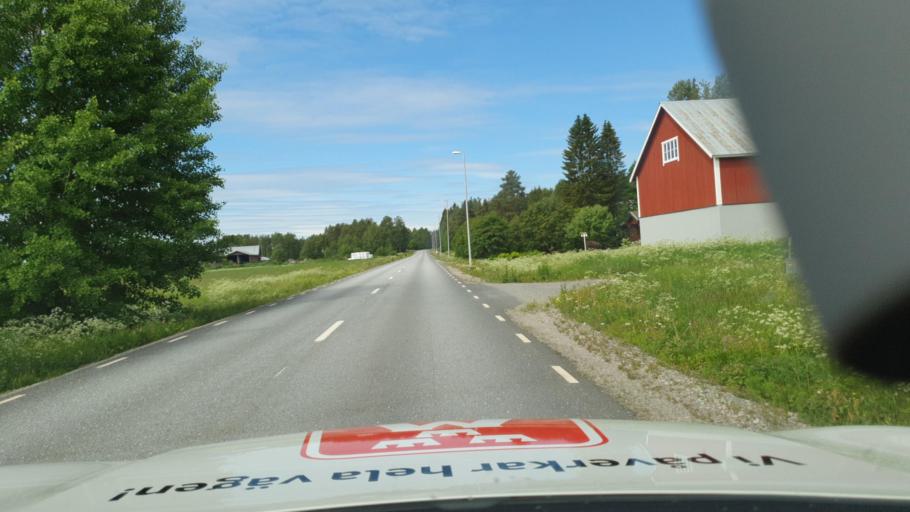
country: SE
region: Vaesterbotten
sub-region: Skelleftea Kommun
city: Forsbacka
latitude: 64.6883
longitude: 20.5157
